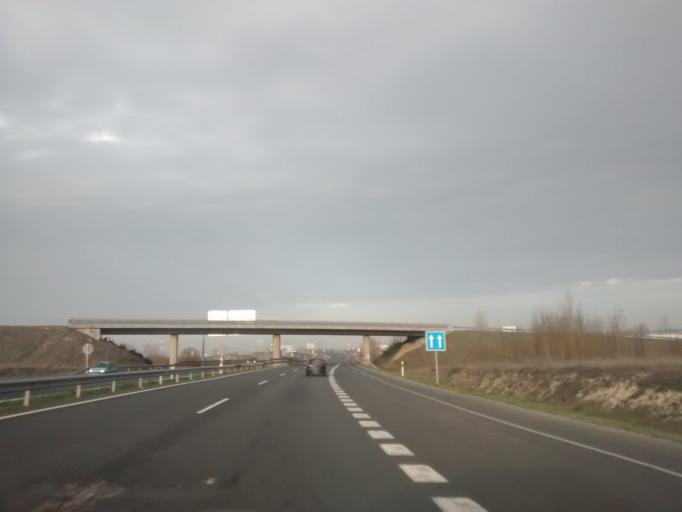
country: ES
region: Basque Country
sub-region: Provincia de Alava
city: Gasteiz / Vitoria
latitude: 42.8462
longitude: -2.7502
